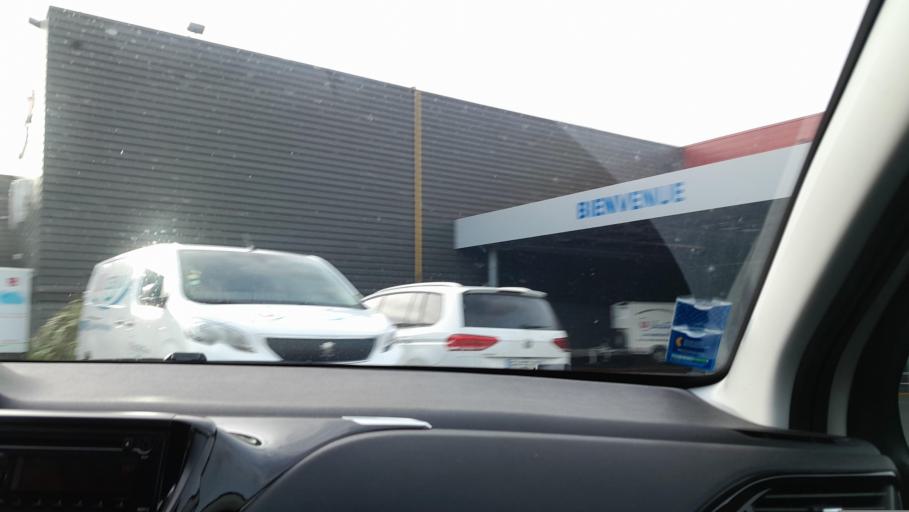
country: FR
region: Brittany
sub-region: Departement d'Ille-et-Vilaine
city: La Guerche-de-Bretagne
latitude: 47.9356
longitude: -1.2349
